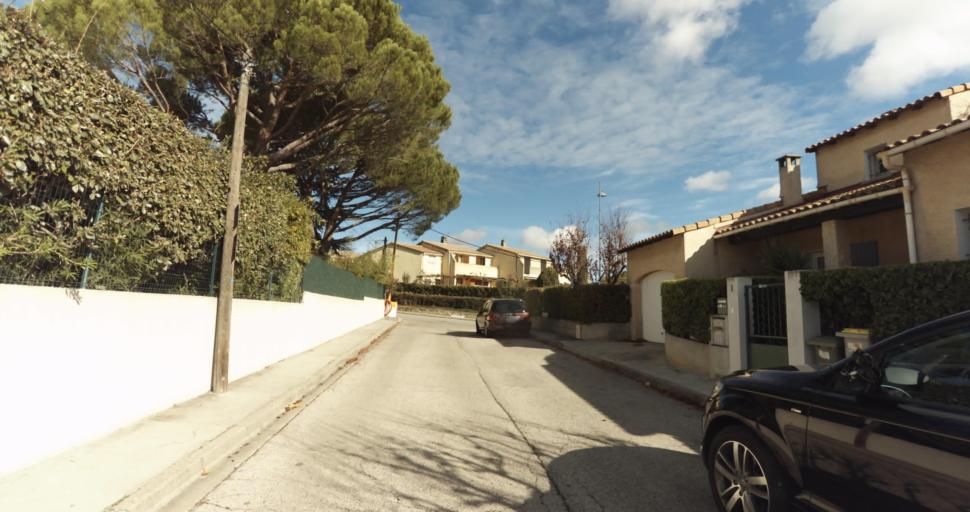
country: FR
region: Provence-Alpes-Cote d'Azur
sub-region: Departement des Bouches-du-Rhone
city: Venelles
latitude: 43.5953
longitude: 5.4825
